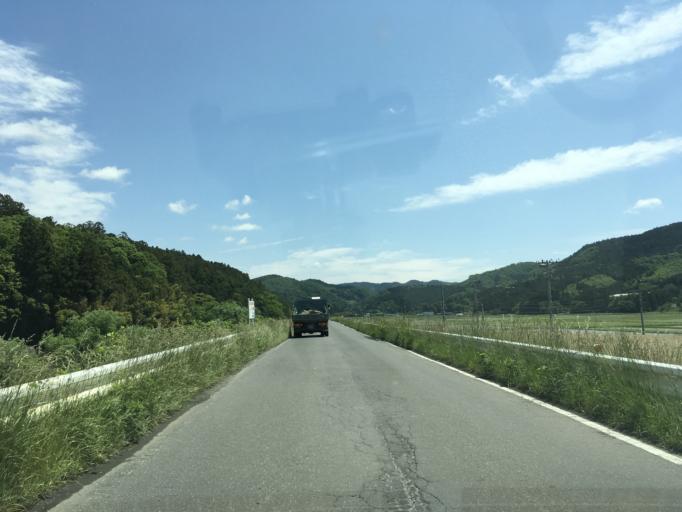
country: JP
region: Miyagi
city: Wakuya
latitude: 38.6550
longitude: 141.2896
